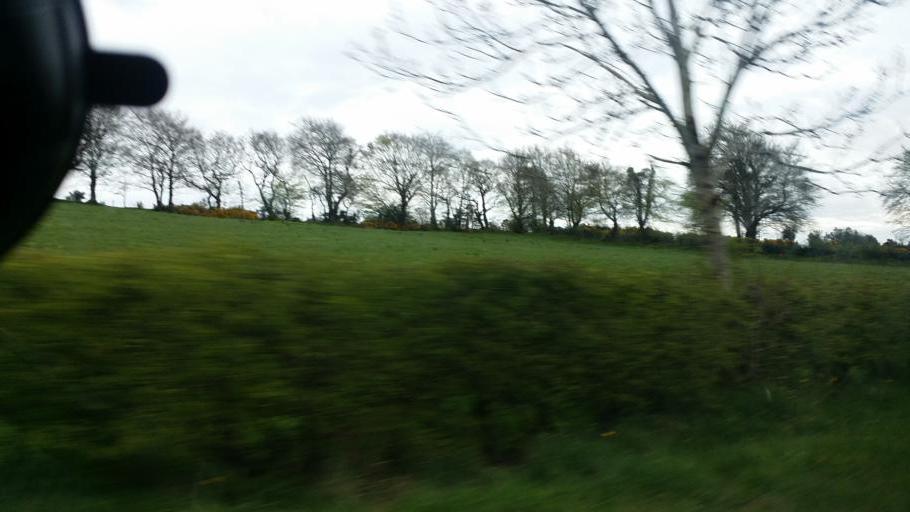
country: IE
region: Ulster
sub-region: An Cabhan
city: Ballyconnell
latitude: 54.1076
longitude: -7.5729
